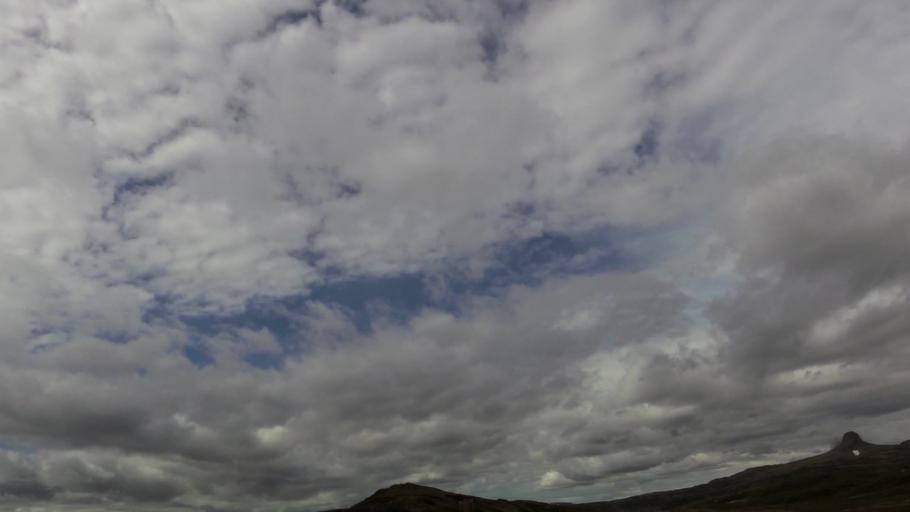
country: IS
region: West
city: Stykkisholmur
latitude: 65.5375
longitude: -22.0963
